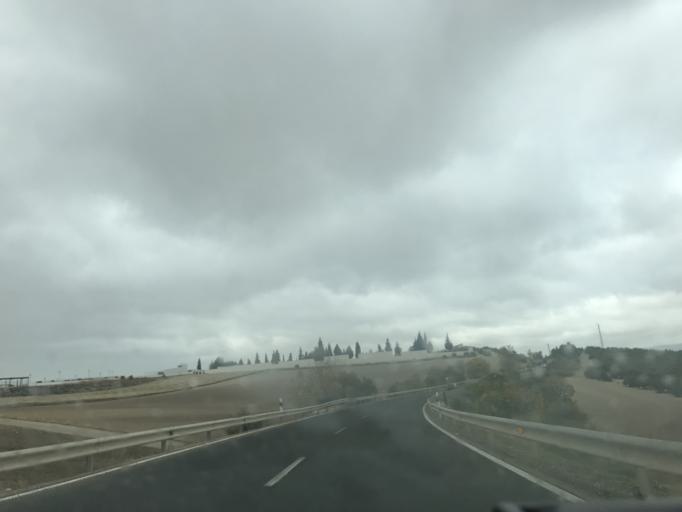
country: ES
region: Andalusia
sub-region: Provincia de Jaen
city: Peal de Becerro
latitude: 37.9176
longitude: -3.1151
